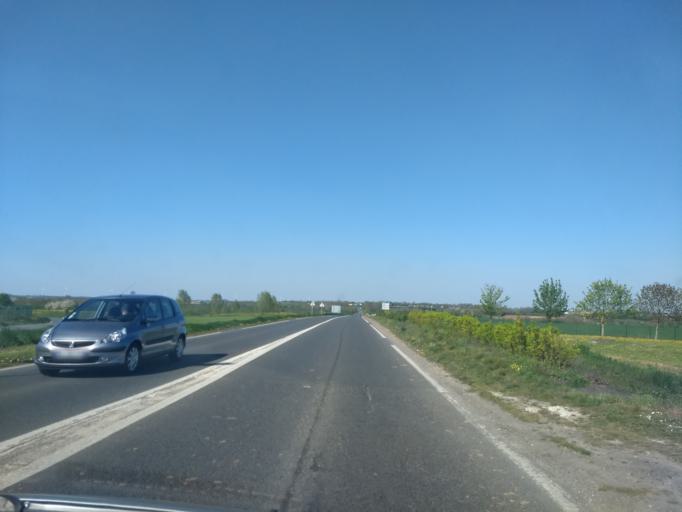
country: FR
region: Picardie
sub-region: Departement de la Somme
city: Villers-Bocage
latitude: 50.0044
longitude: 2.3128
